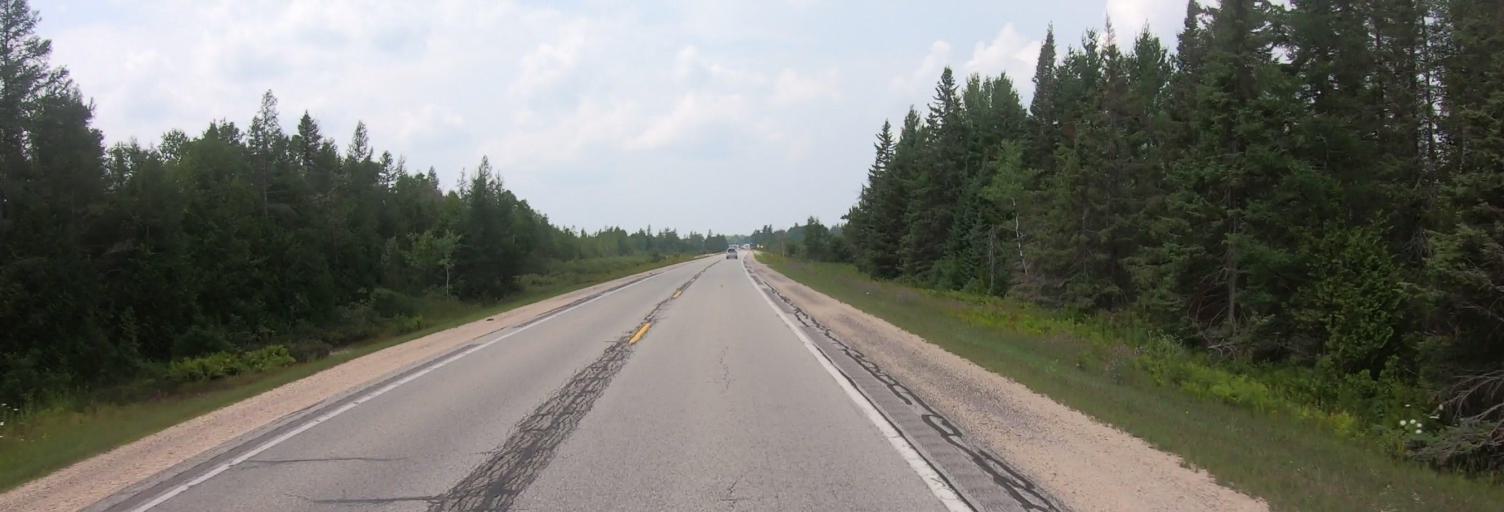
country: US
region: Michigan
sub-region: Alger County
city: Munising
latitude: 46.3474
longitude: -86.4566
